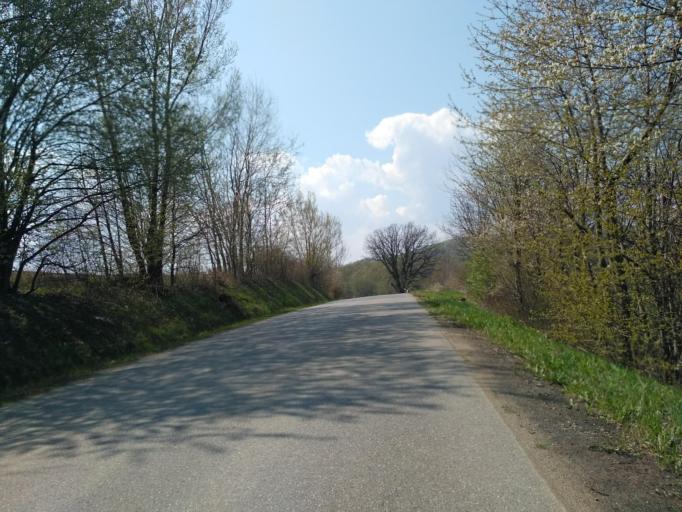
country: PL
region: Subcarpathian Voivodeship
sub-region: Powiat sanocki
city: Zarszyn
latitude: 49.5627
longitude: 21.9973
